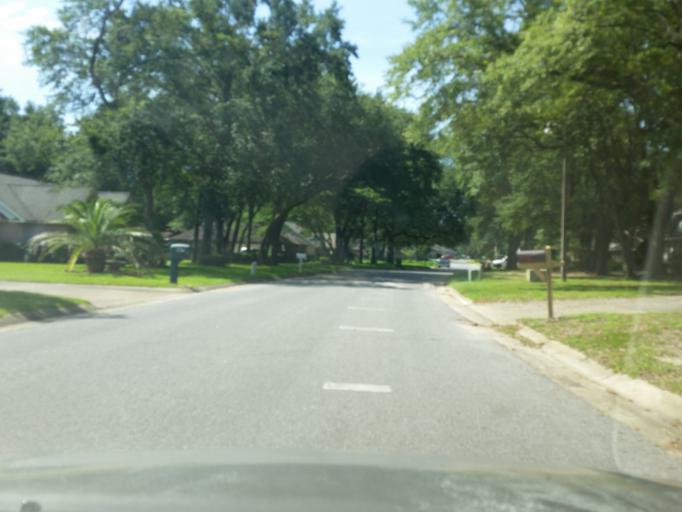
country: US
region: Florida
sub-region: Escambia County
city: Ferry Pass
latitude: 30.5193
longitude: -87.2062
